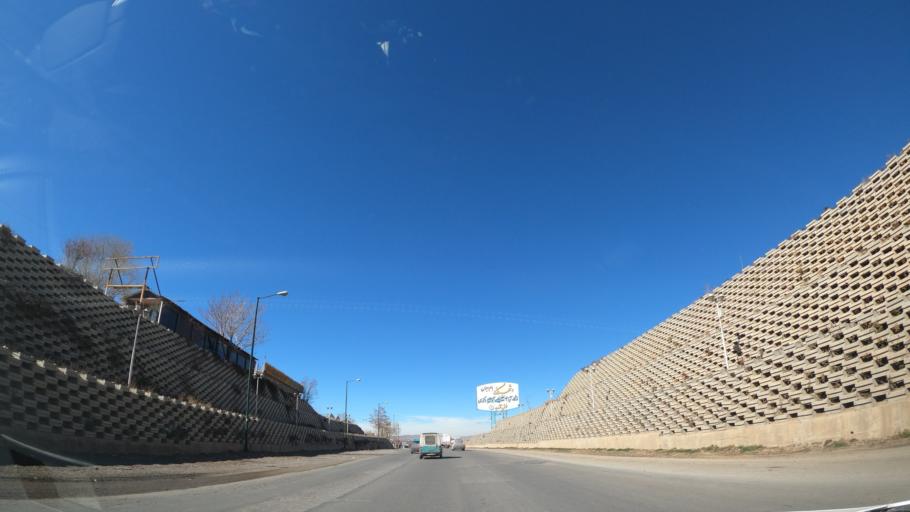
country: IR
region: Chahar Mahall va Bakhtiari
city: Shahrekord
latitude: 32.3071
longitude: 50.9068
